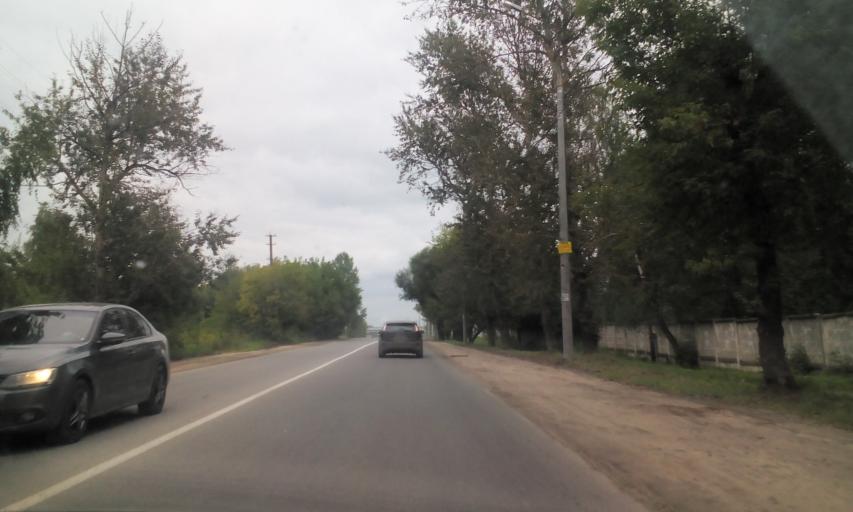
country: RU
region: Kaluga
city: Kaluga
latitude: 54.5156
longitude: 36.3189
